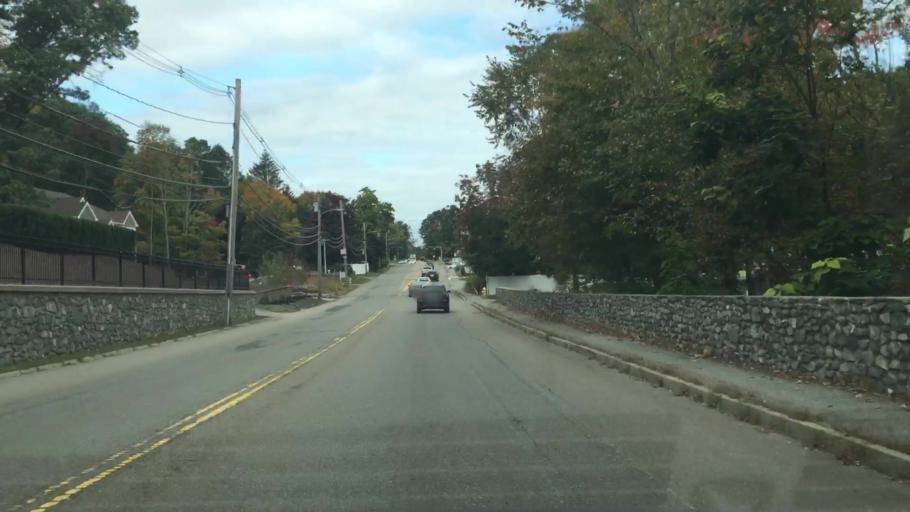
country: US
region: Massachusetts
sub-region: Essex County
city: Middleton
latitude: 42.5975
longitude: -71.0189
